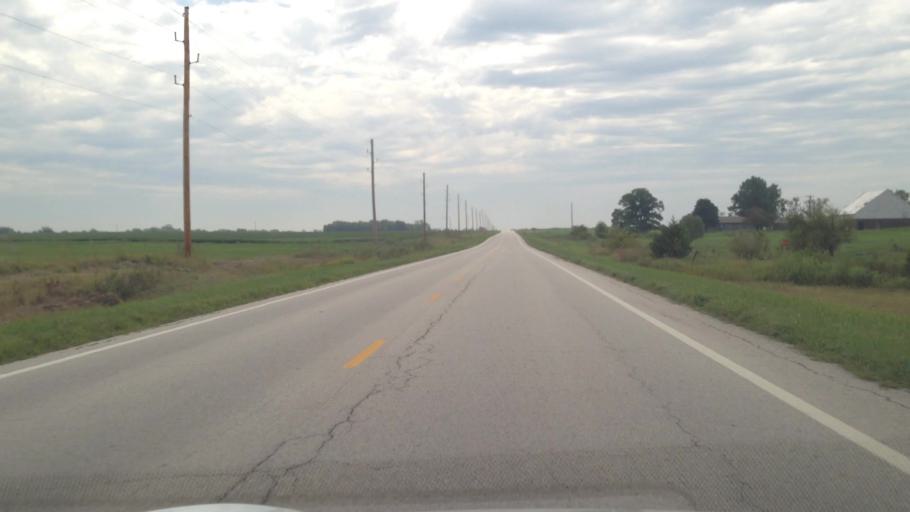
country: US
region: Kansas
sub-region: Allen County
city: Iola
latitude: 37.9426
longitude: -95.1700
